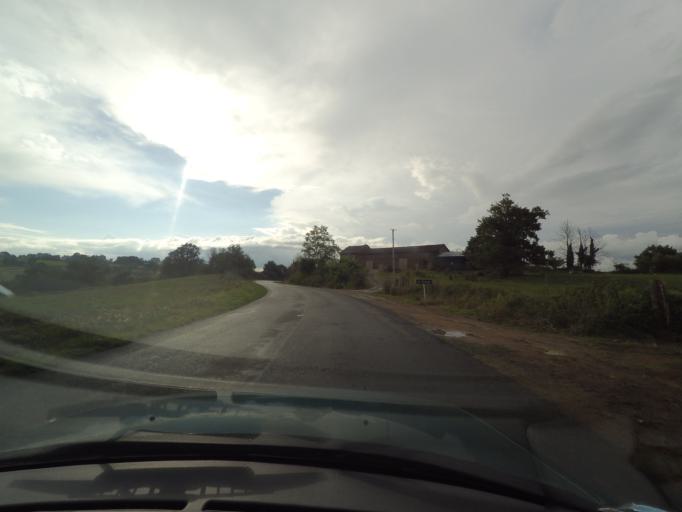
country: FR
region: Limousin
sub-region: Departement de la Haute-Vienne
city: Nexon
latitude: 45.7097
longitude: 1.1604
